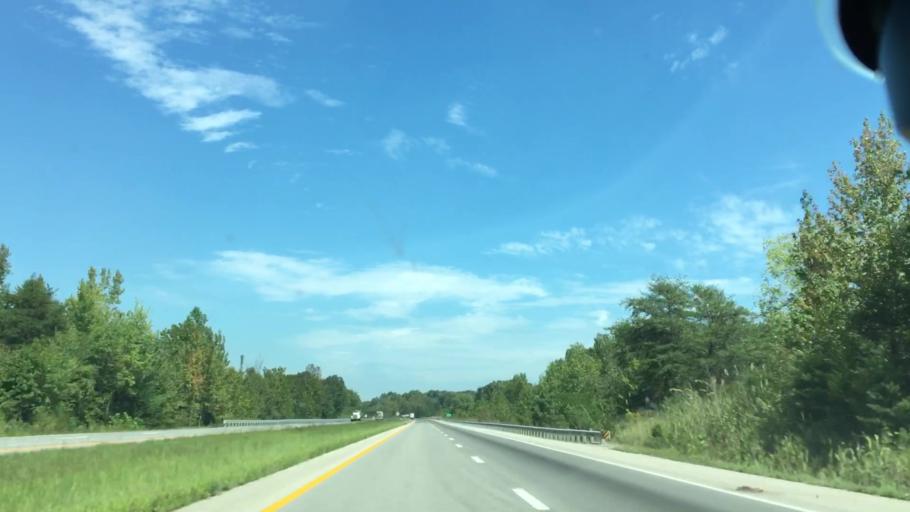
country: US
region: Kentucky
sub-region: Hopkins County
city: Nortonville
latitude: 37.1683
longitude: -87.4524
